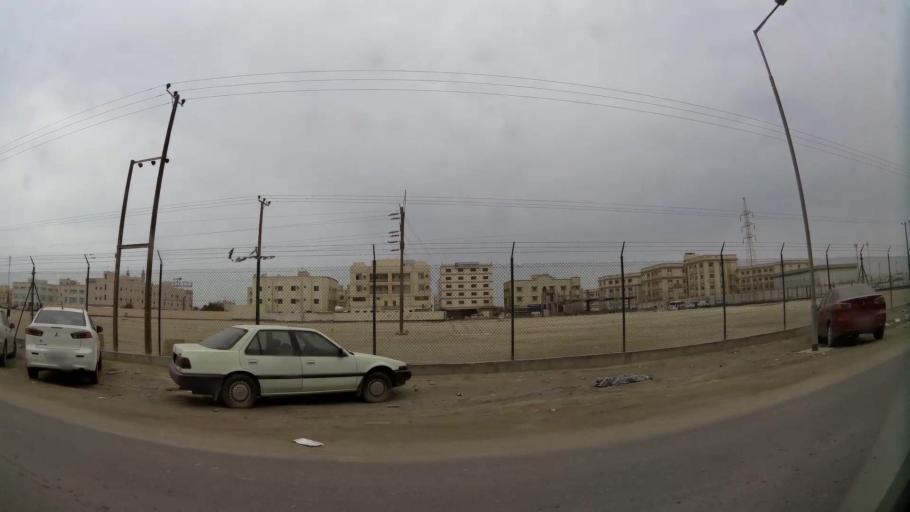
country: BH
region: Northern
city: Madinat `Isa
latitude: 26.1810
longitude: 50.5346
